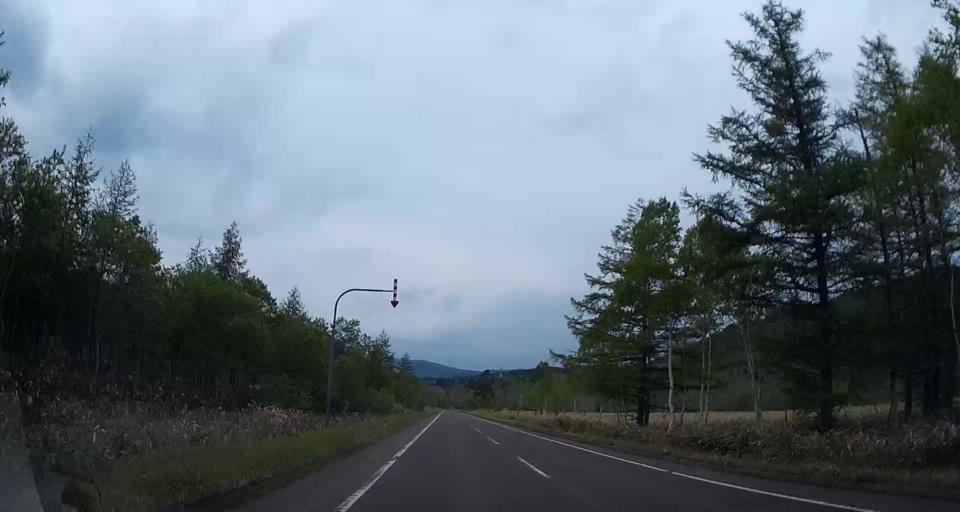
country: JP
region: Hokkaido
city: Shiraoi
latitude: 42.6765
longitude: 141.1462
